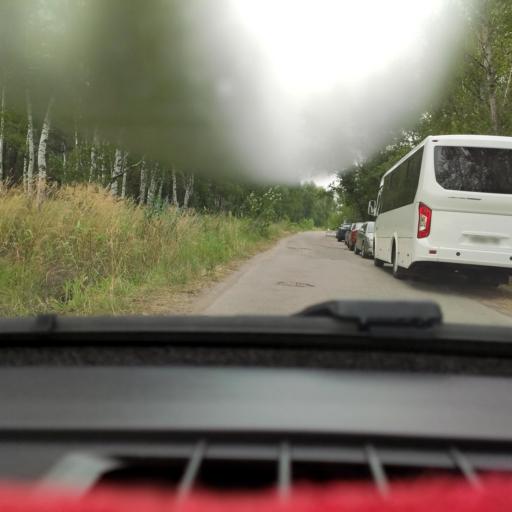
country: RU
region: Voronezj
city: Somovo
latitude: 51.7319
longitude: 39.3196
